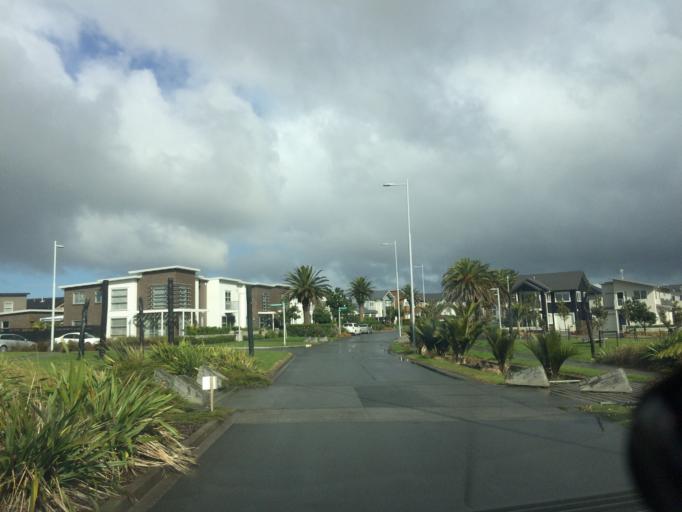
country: NZ
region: Auckland
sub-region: Auckland
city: Rosebank
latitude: -36.7911
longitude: 174.6597
